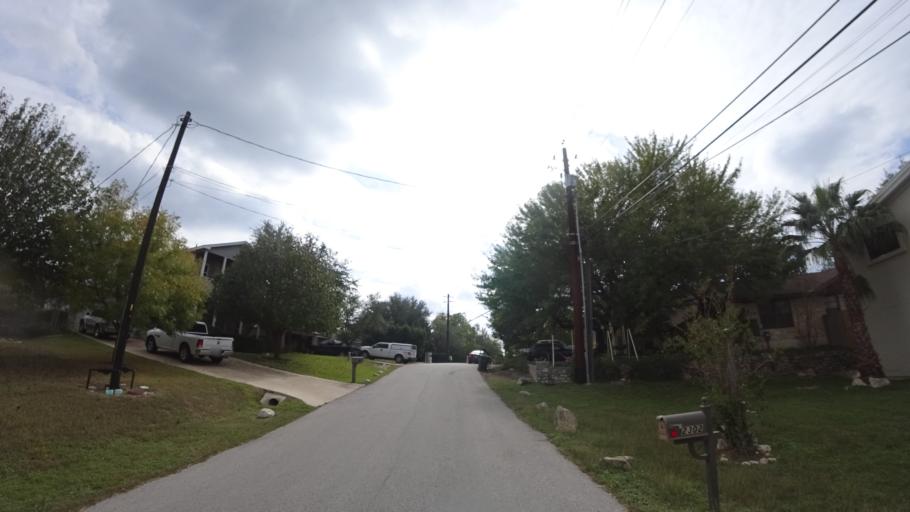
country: US
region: Texas
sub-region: Travis County
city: Hudson Bend
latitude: 30.3749
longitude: -97.9196
